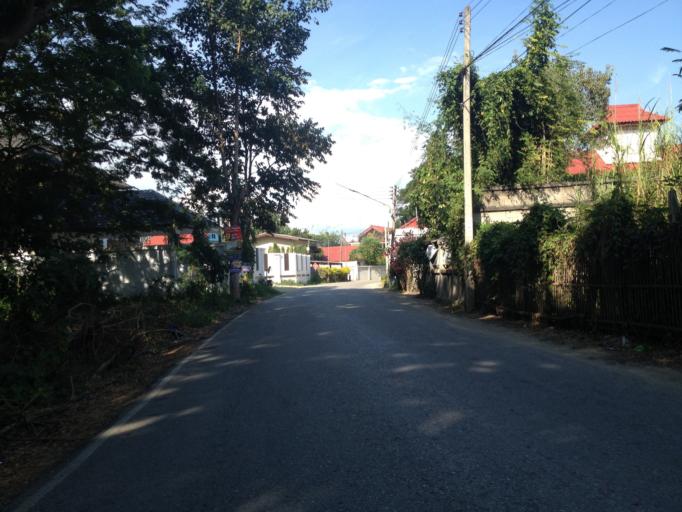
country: TH
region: Chiang Mai
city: Chiang Mai
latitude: 18.7540
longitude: 98.9824
